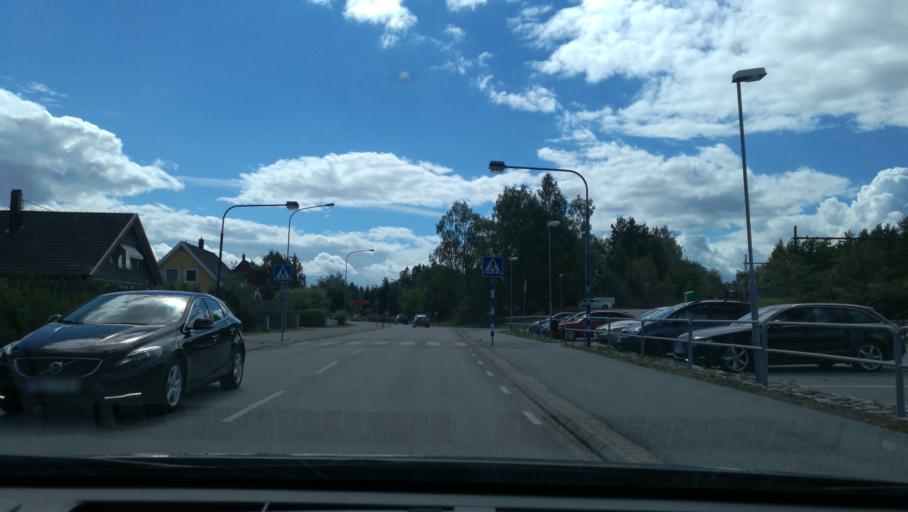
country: SE
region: OEstergoetland
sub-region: Norrkopings Kommun
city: Krokek
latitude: 58.6734
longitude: 16.3639
